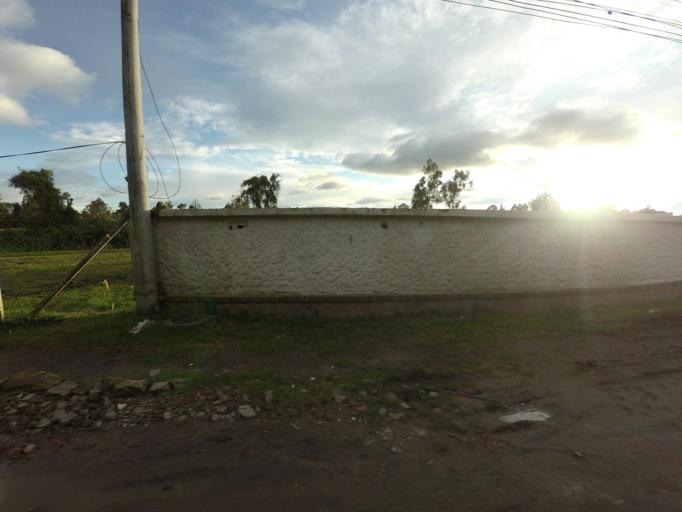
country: CO
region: Cundinamarca
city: Chia
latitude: 4.8177
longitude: -74.0308
